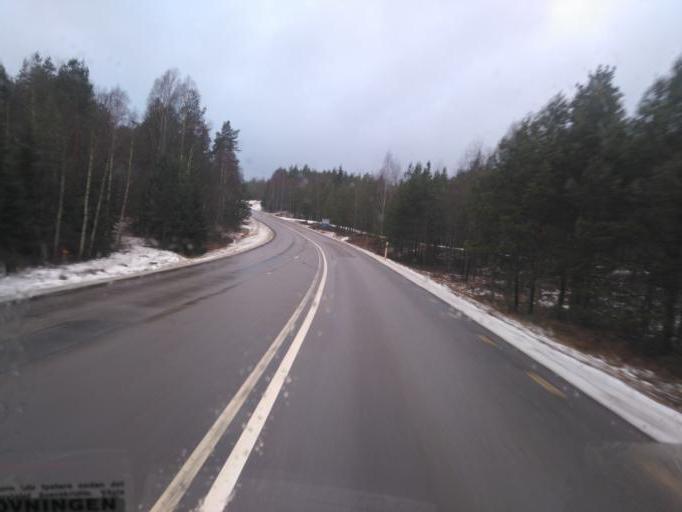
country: SE
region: Joenkoeping
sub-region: Eksjo Kommun
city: Mariannelund
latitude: 57.6264
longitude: 15.6107
